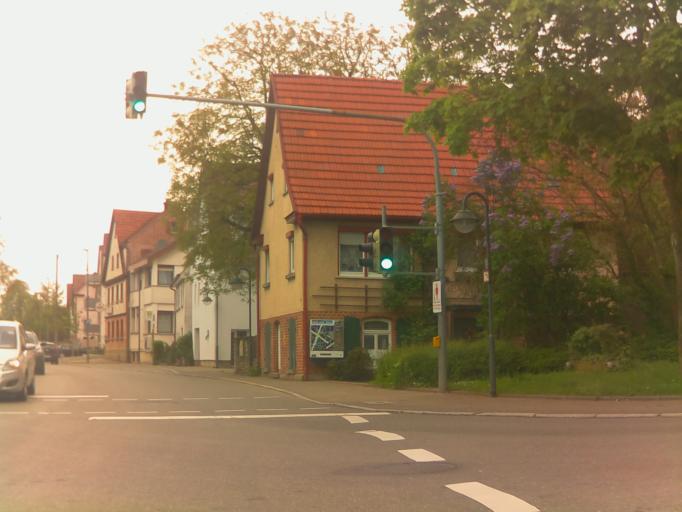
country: DE
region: Baden-Wuerttemberg
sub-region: Tuebingen Region
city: Pliezhausen
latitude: 48.5762
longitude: 9.1819
